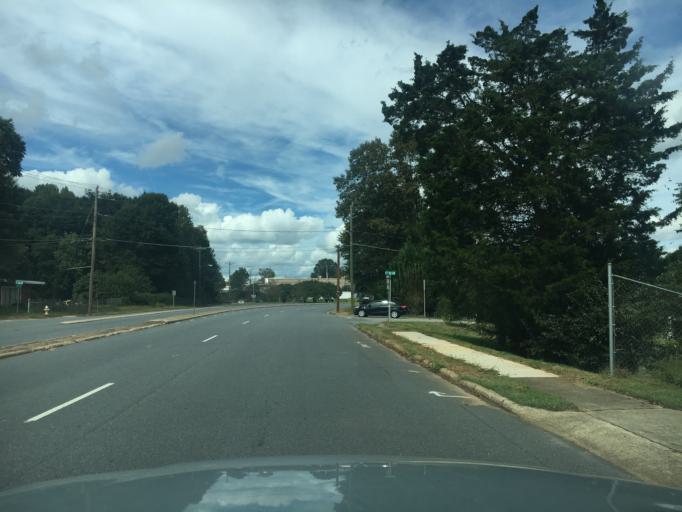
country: US
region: North Carolina
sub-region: Catawba County
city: Longview
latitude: 35.7258
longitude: -81.3625
